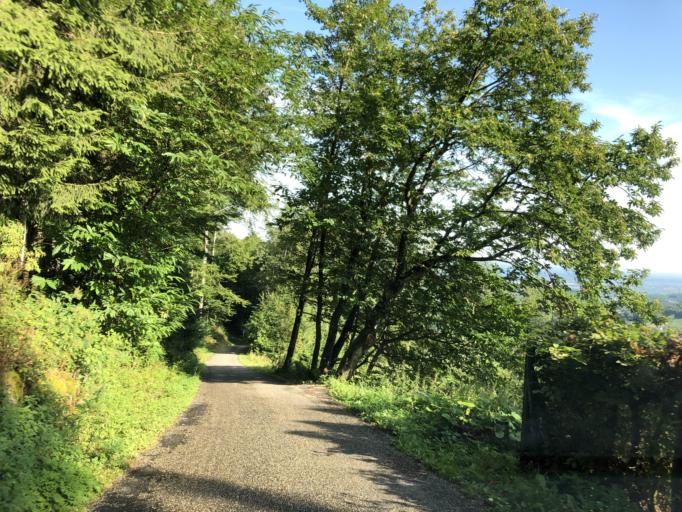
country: DE
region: Baden-Wuerttemberg
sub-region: Freiburg Region
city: Sasbachwalden
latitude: 48.6270
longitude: 8.1502
